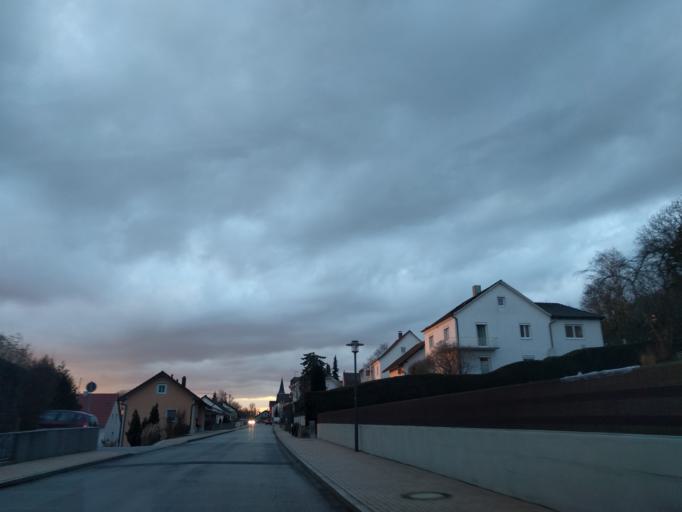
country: DE
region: Bavaria
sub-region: Lower Bavaria
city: Winzer
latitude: 48.7201
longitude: 13.0821
